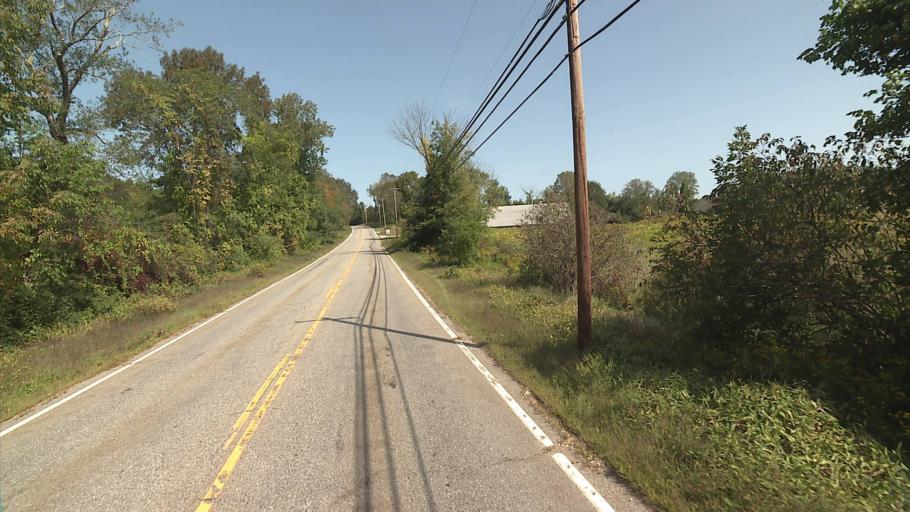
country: US
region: Connecticut
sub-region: Windham County
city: Putnam
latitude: 41.8618
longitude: -71.9592
